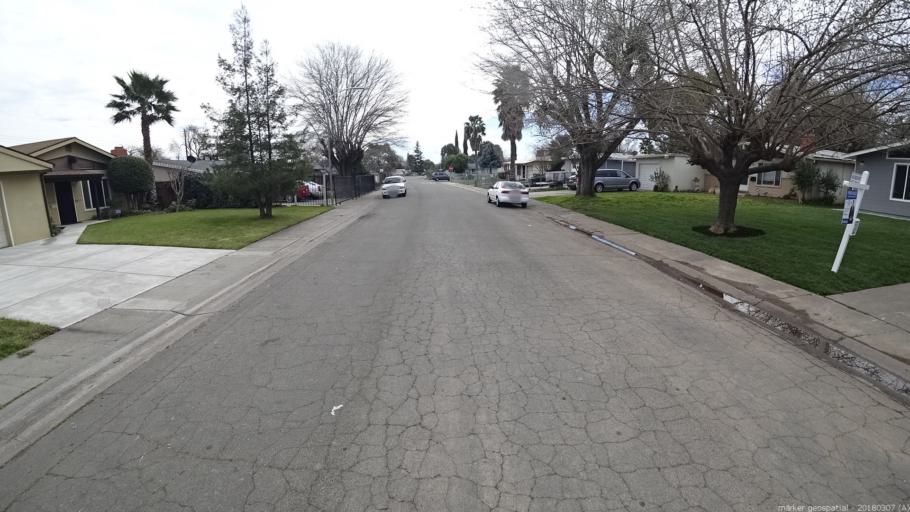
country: US
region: California
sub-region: Sacramento County
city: Parkway
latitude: 38.5199
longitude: -121.4573
